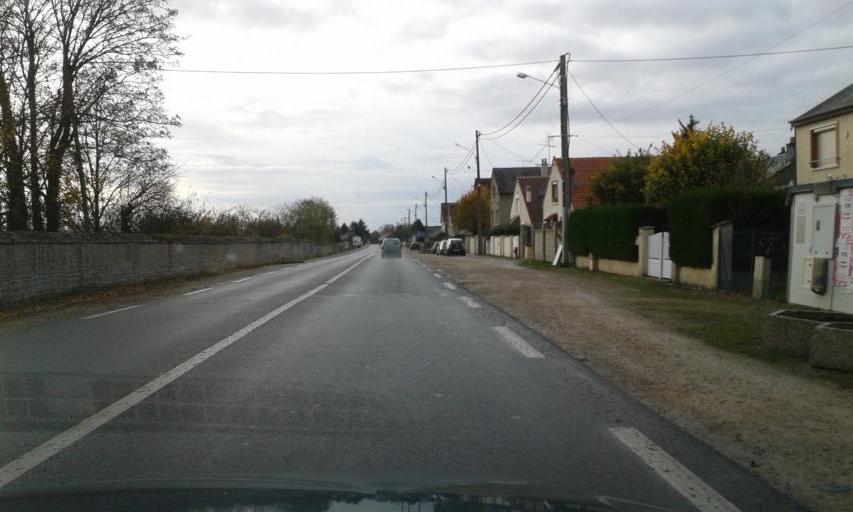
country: FR
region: Centre
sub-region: Departement du Loiret
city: Saint-Ay
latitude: 47.8632
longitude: 1.7640
